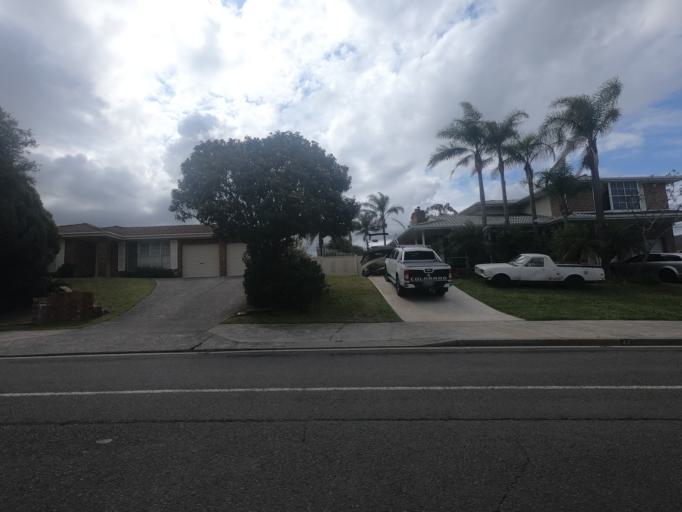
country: AU
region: New South Wales
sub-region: Wollongong
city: Dapto
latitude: -34.4934
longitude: 150.7809
